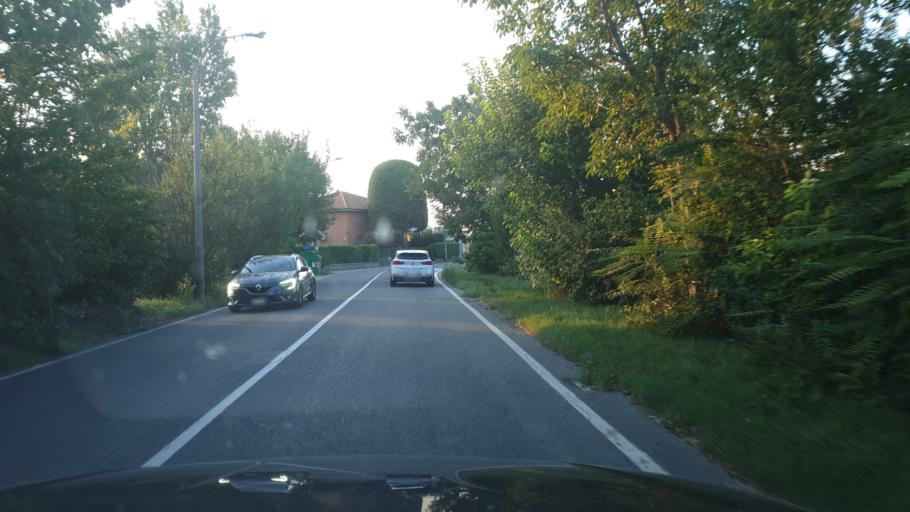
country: IT
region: Emilia-Romagna
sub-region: Provincia di Bologna
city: Quarto Inferiore
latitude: 44.5185
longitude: 11.3816
